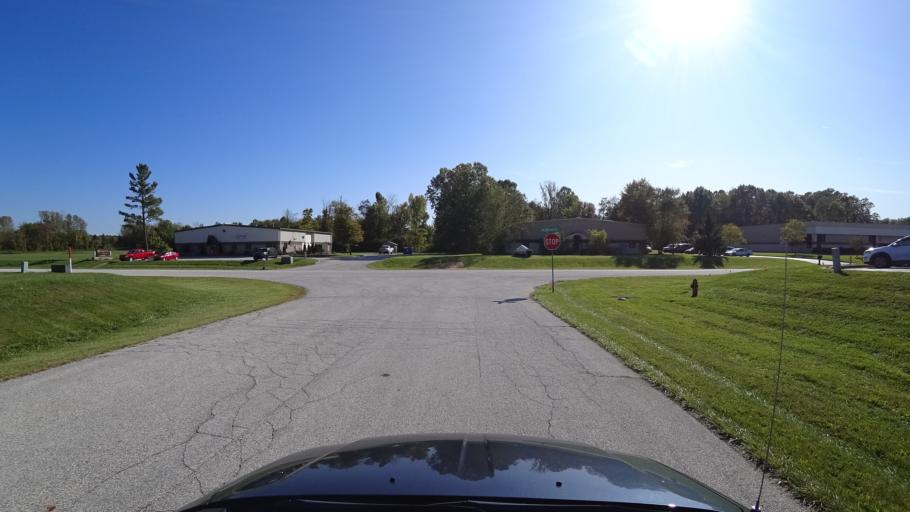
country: US
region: Indiana
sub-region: LaPorte County
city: Trail Creek
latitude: 41.6967
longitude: -86.8389
